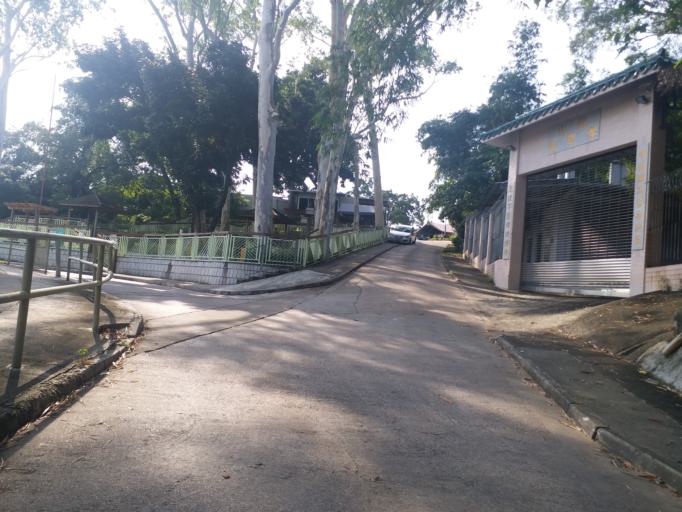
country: HK
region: Yuen Long
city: Yuen Long Kau Hui
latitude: 22.4440
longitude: 114.0101
